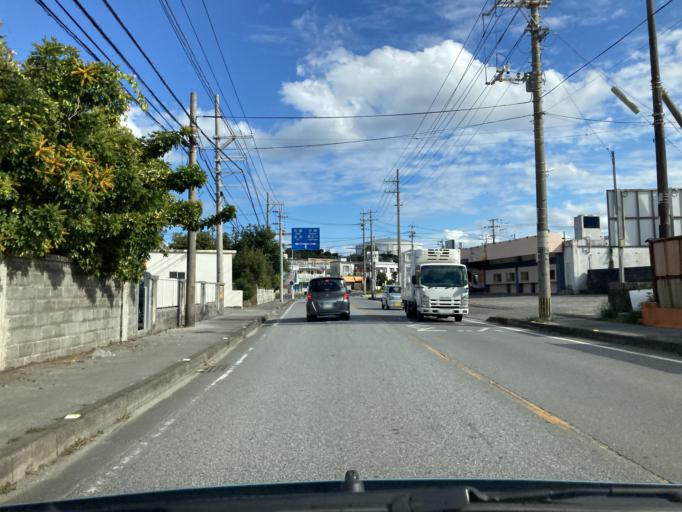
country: JP
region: Okinawa
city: Ishikawa
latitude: 26.4112
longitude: 127.8260
